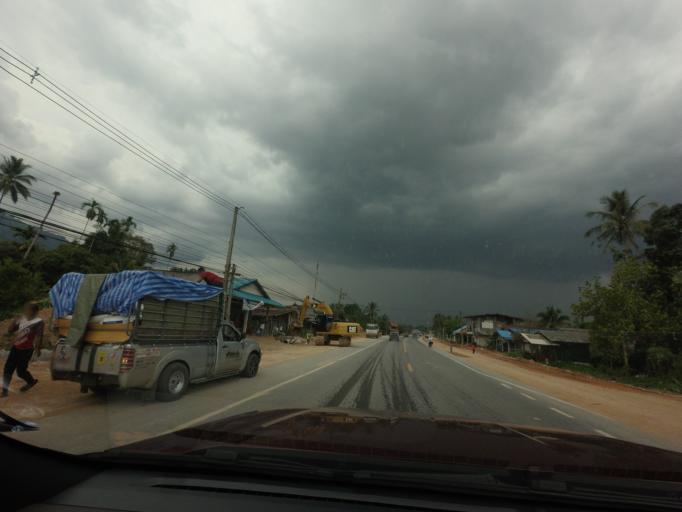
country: TH
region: Yala
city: Krong Pi Nang
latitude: 6.4307
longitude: 101.2784
